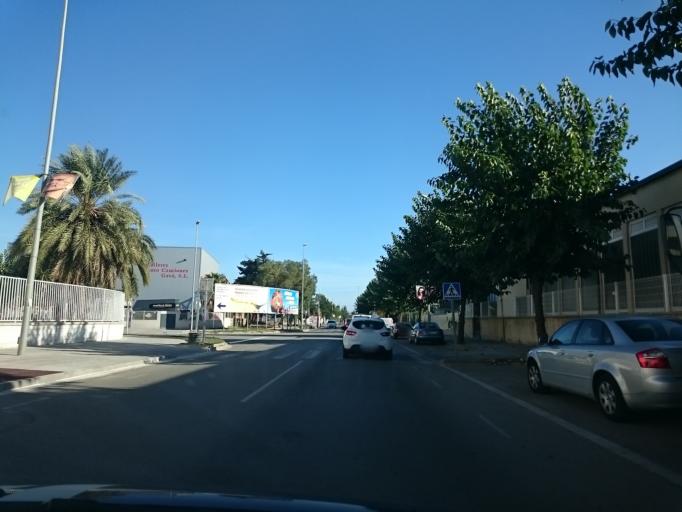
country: ES
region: Catalonia
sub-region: Provincia de Barcelona
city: Gava
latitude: 41.2975
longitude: 2.0107
